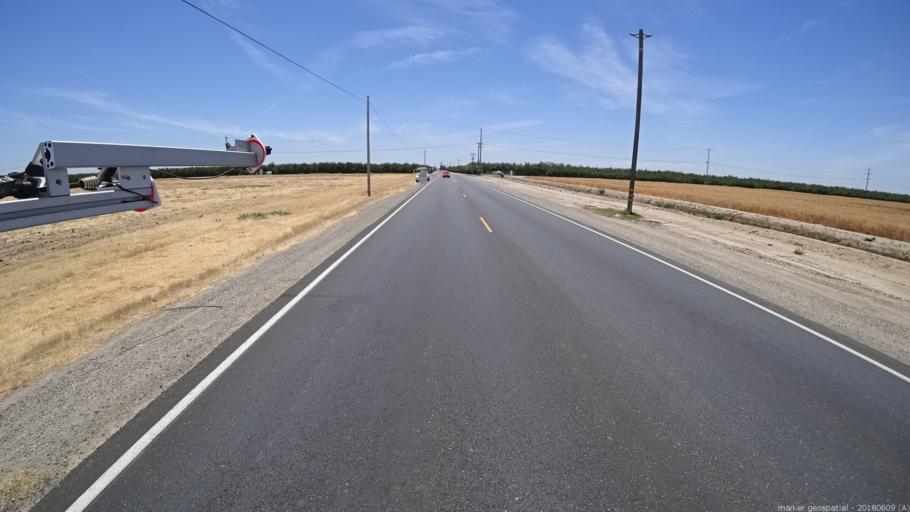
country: US
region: California
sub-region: Madera County
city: Parkwood
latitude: 36.9251
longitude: -120.0924
